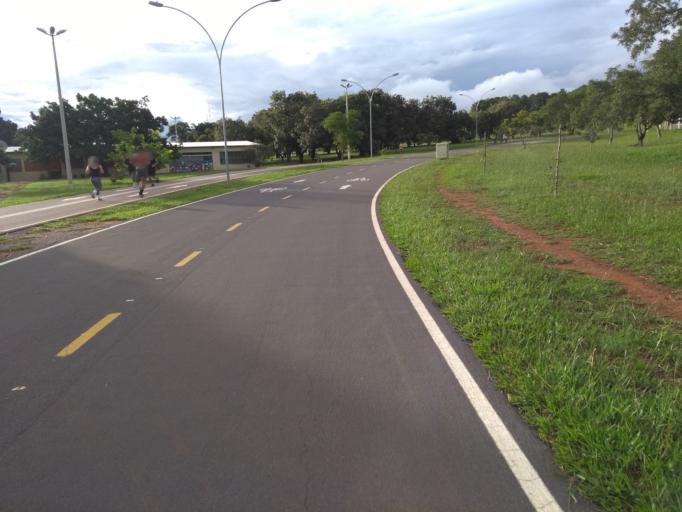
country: BR
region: Federal District
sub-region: Brasilia
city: Brasilia
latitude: -15.8105
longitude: -47.9246
